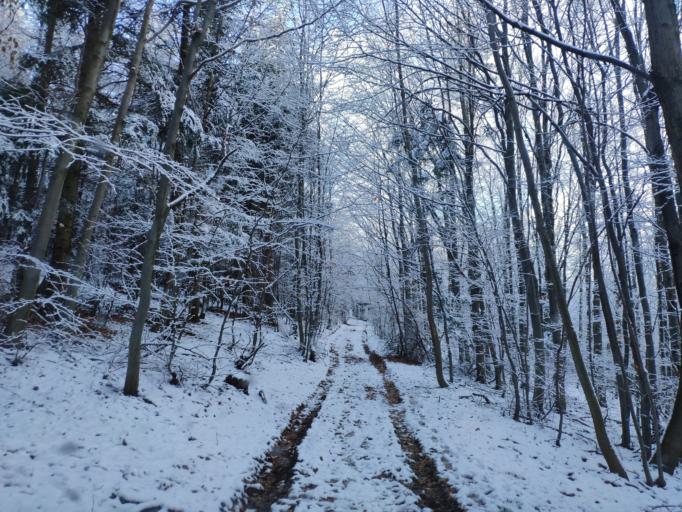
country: SK
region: Kosicky
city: Moldava nad Bodvou
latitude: 48.7434
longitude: 21.0912
